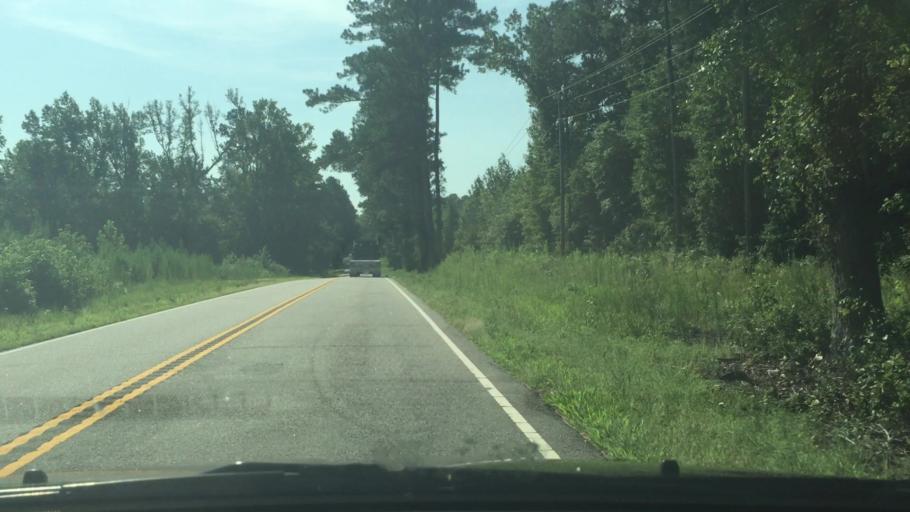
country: US
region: Virginia
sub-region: Sussex County
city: Sussex
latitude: 37.0167
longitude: -77.2822
